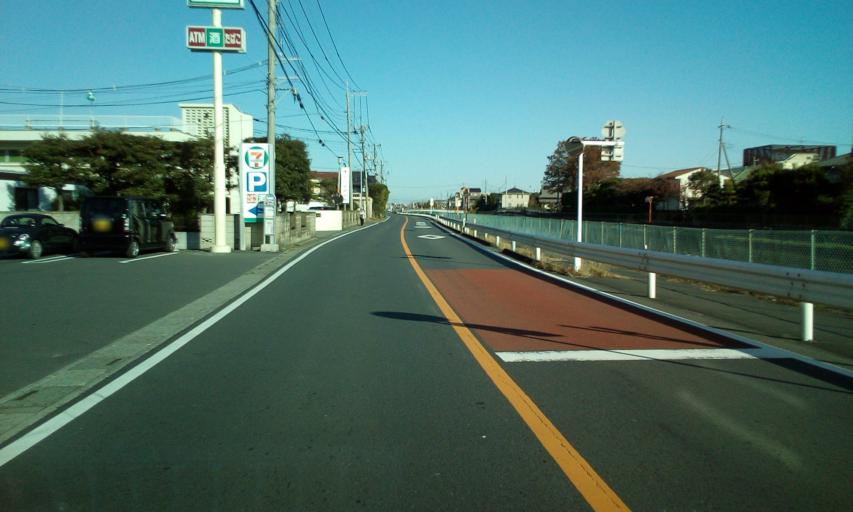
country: JP
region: Chiba
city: Matsudo
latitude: 35.8032
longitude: 139.8841
